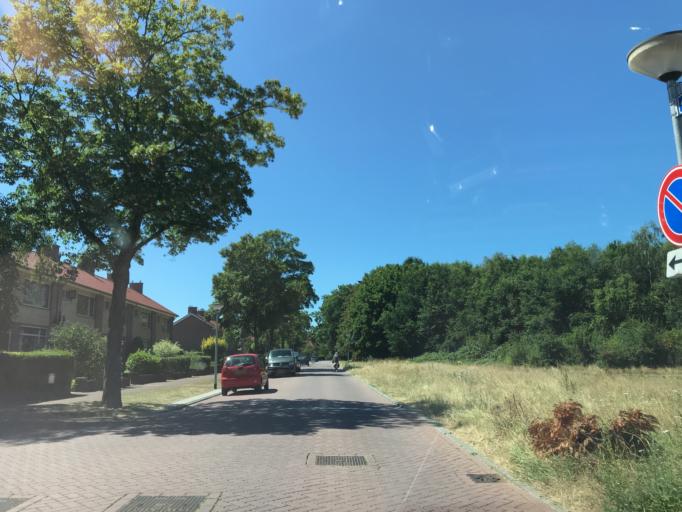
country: NL
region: North Holland
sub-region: Gemeente Huizen
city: Huizen
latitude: 52.2999
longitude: 5.2222
